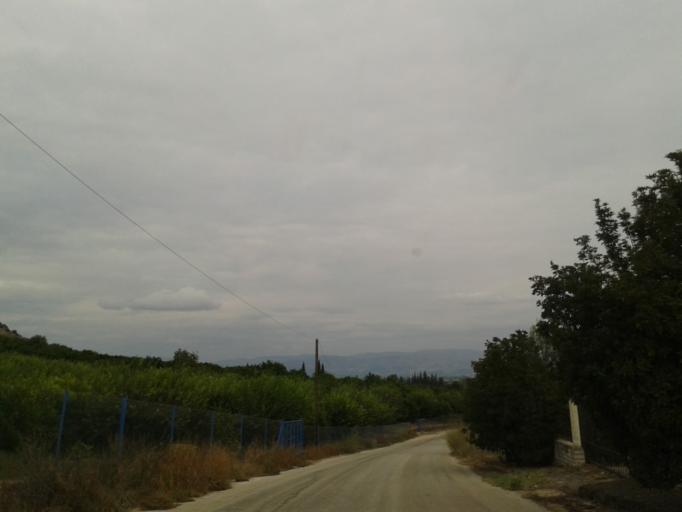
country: GR
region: Peloponnese
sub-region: Nomos Argolidos
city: Nea Kios
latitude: 37.5911
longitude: 22.6820
